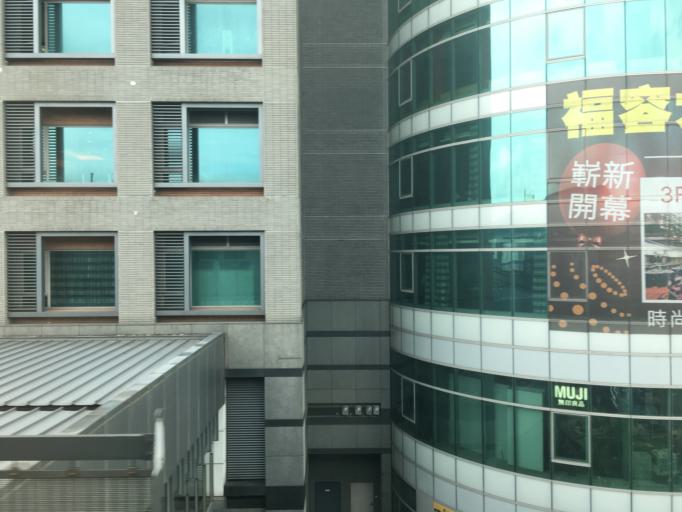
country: TW
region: Taiwan
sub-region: Taoyuan
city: Taoyuan
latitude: 25.0607
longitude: 121.3703
